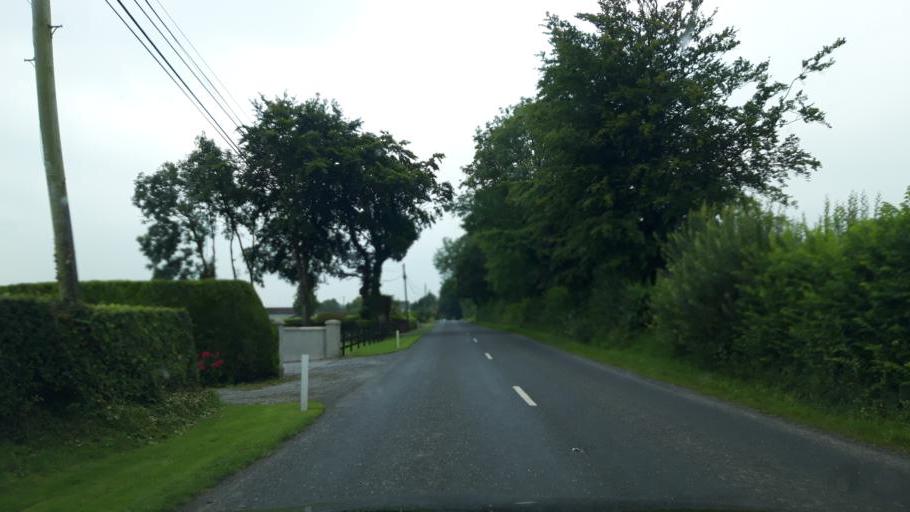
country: IE
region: Munster
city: Fethard
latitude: 52.5463
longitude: -7.6791
